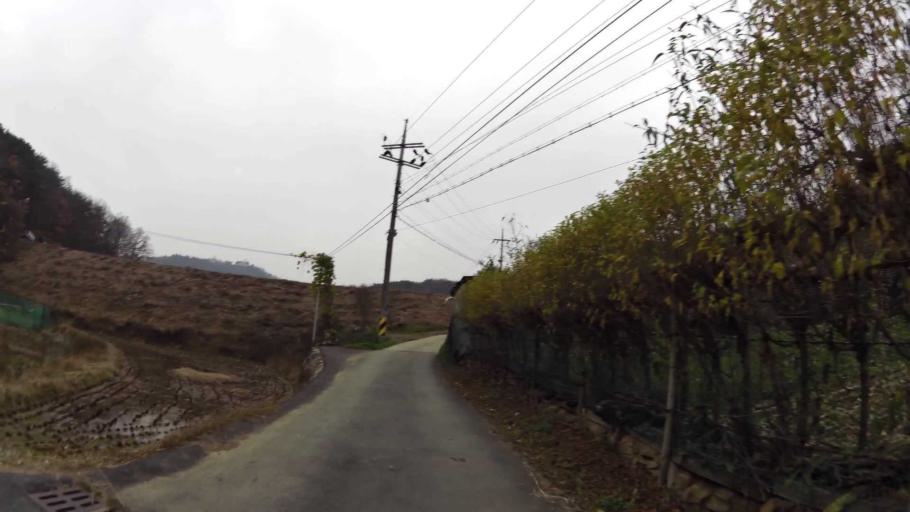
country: KR
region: Daegu
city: Daegu
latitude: 35.8600
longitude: 128.6645
